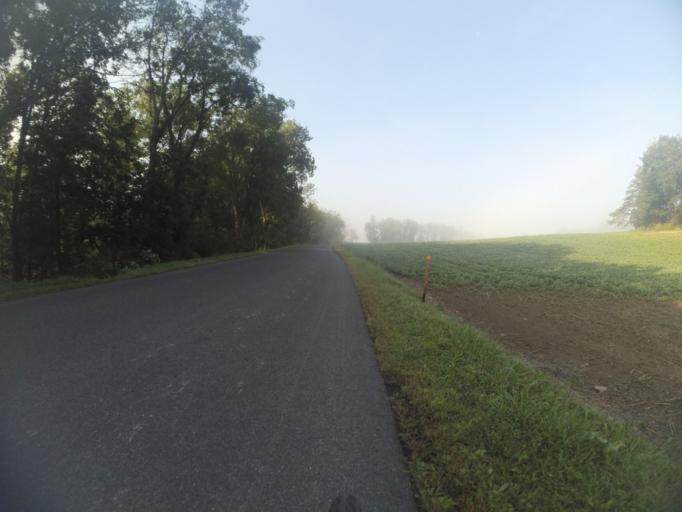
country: US
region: Pennsylvania
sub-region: Centre County
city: Centre Hall
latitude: 40.8735
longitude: -77.5894
